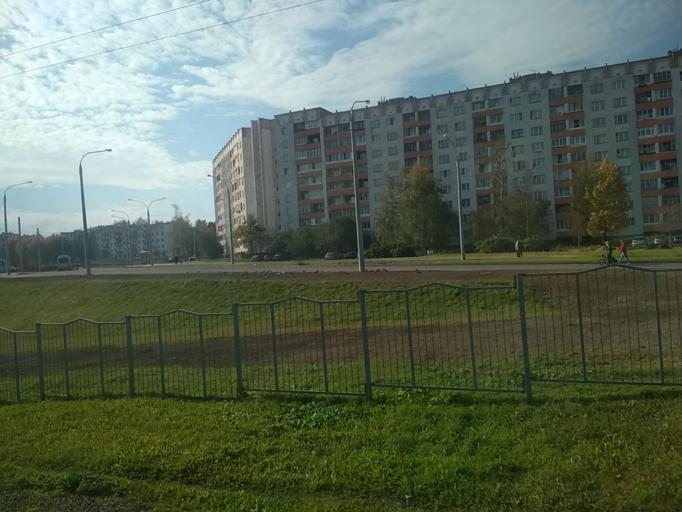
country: BY
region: Minsk
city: Syenitsa
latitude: 53.8524
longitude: 27.5568
